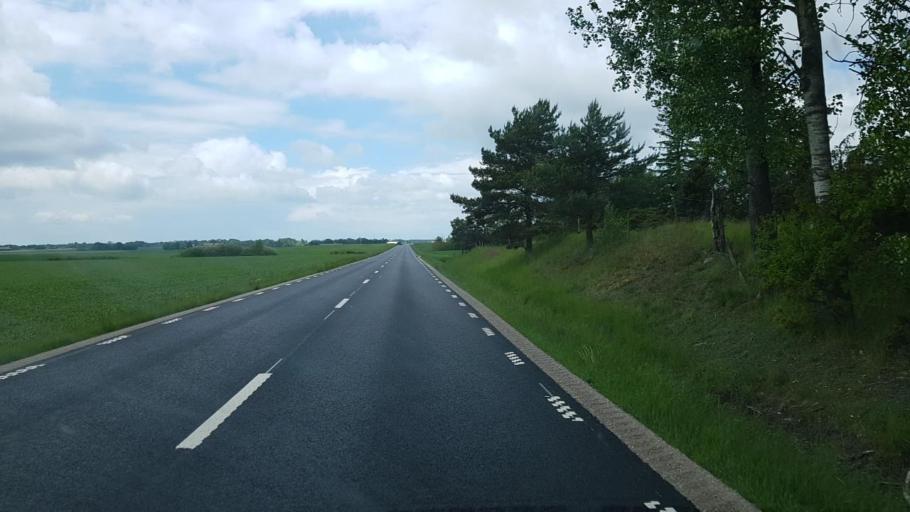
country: SE
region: OEstergoetland
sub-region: Linkopings Kommun
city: Vikingstad
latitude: 58.4840
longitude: 15.3830
